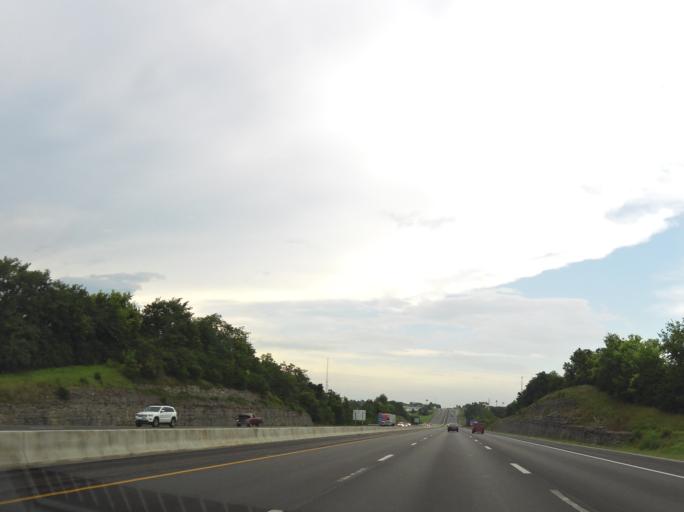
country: US
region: Kentucky
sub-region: Madison County
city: Richmond
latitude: 37.7560
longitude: -84.3191
